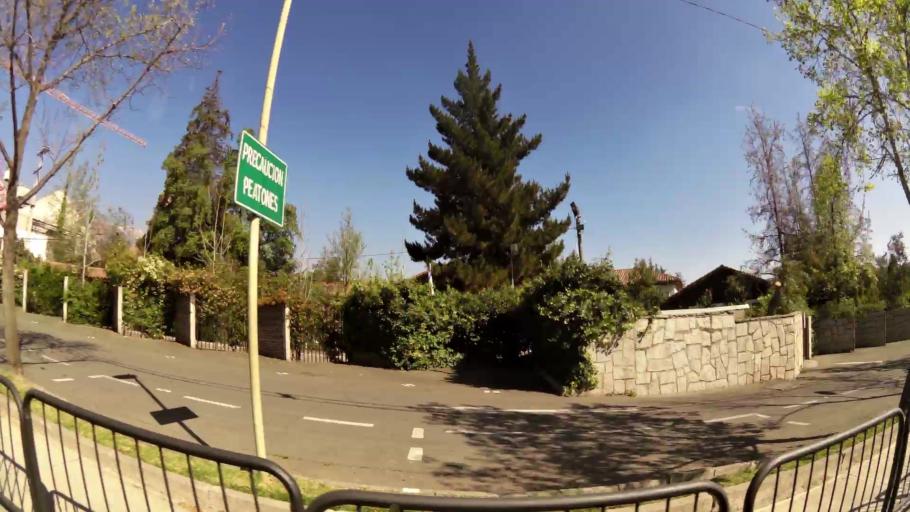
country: CL
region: Santiago Metropolitan
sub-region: Provincia de Santiago
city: Villa Presidente Frei, Nunoa, Santiago, Chile
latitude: -33.4015
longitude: -70.5213
